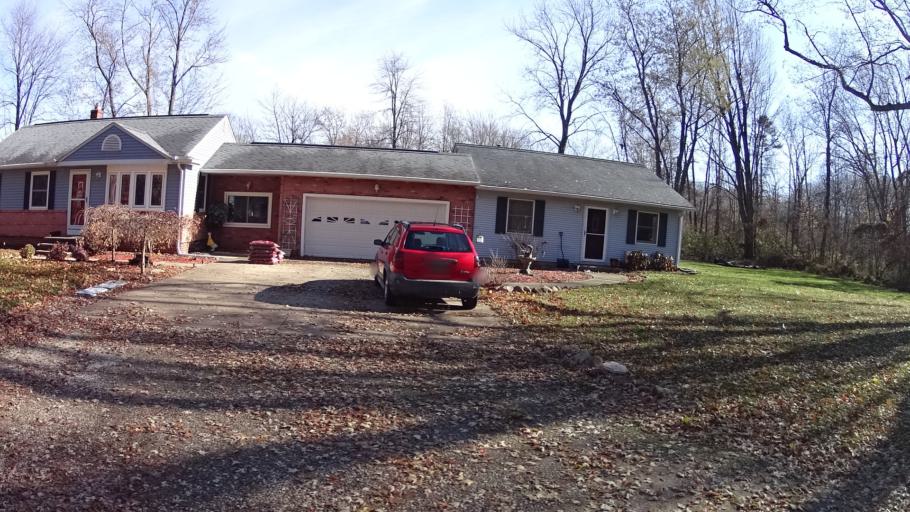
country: US
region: Ohio
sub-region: Lorain County
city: Sheffield Lake
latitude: 41.4945
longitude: -82.0774
